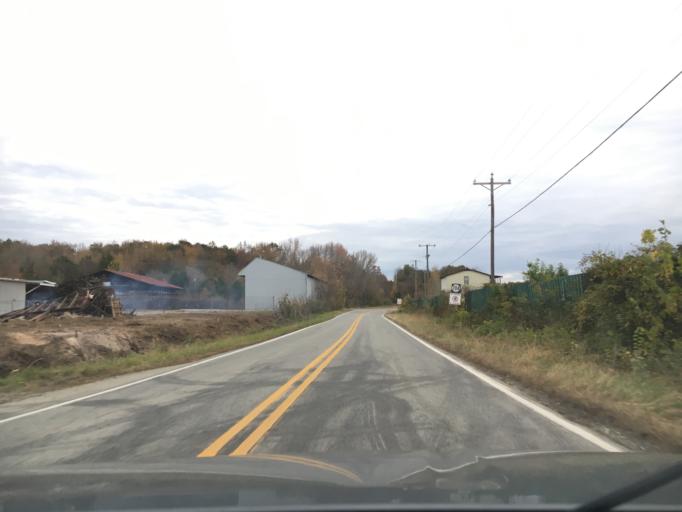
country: US
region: Virginia
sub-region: Halifax County
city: South Boston
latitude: 36.6846
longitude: -78.9072
